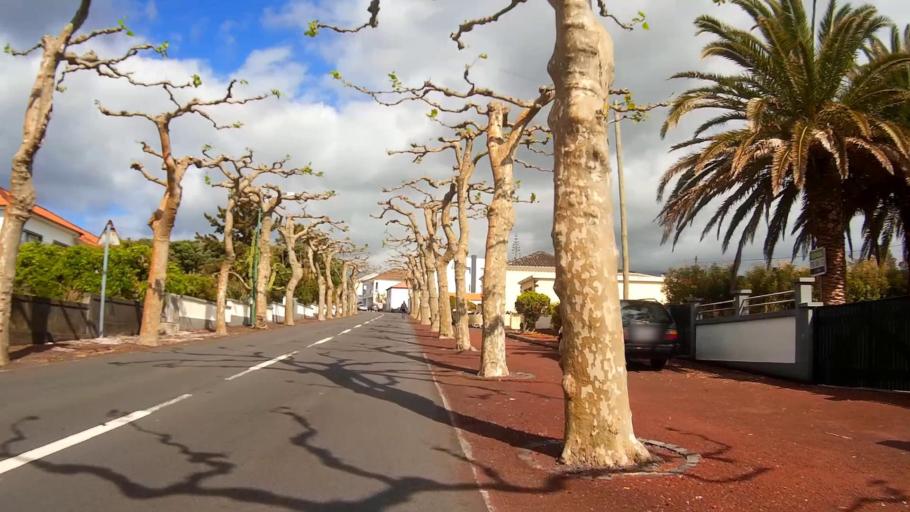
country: PT
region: Azores
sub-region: Madalena
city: Madalena
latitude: 38.5349
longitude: -28.5242
